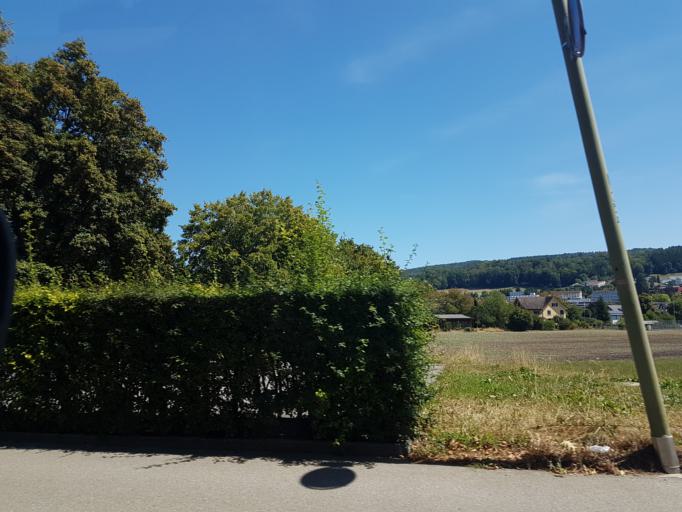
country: CH
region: Zurich
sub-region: Bezirk Affoltern
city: Affoltern / Unterdorf
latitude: 47.2829
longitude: 8.4463
